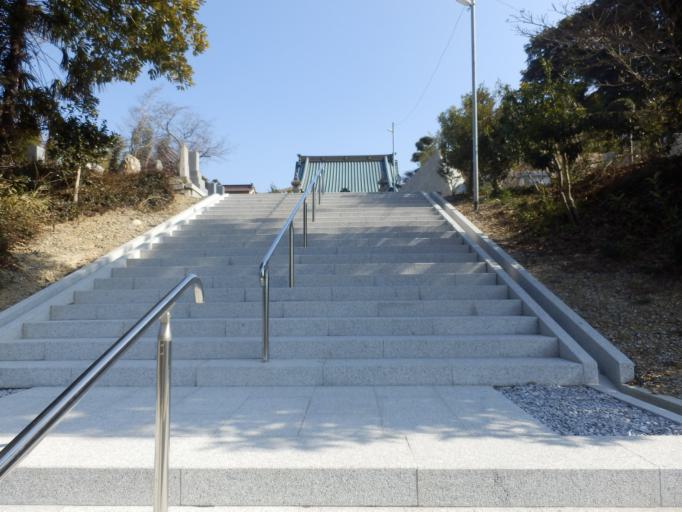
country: JP
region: Shizuoka
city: Kosai-shi
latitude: 34.7192
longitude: 137.5253
